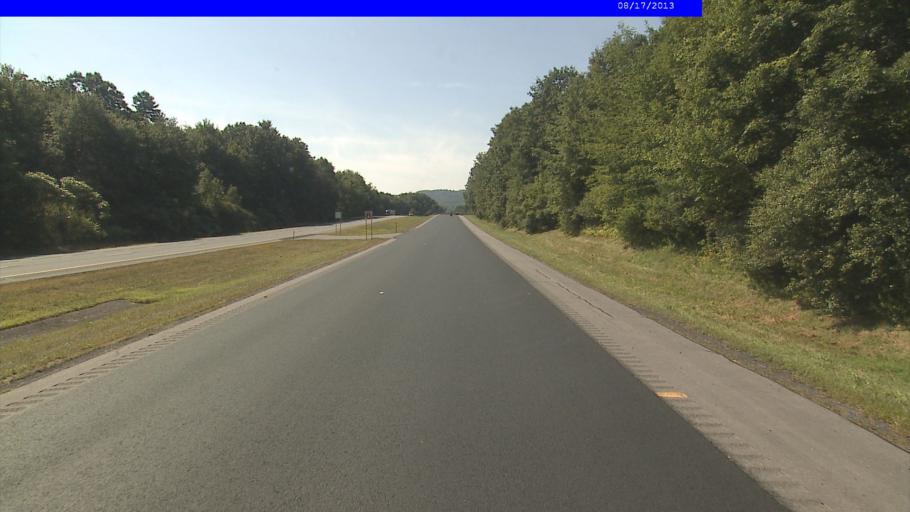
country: US
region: New Hampshire
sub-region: Cheshire County
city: Westmoreland
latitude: 42.9821
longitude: -72.4814
